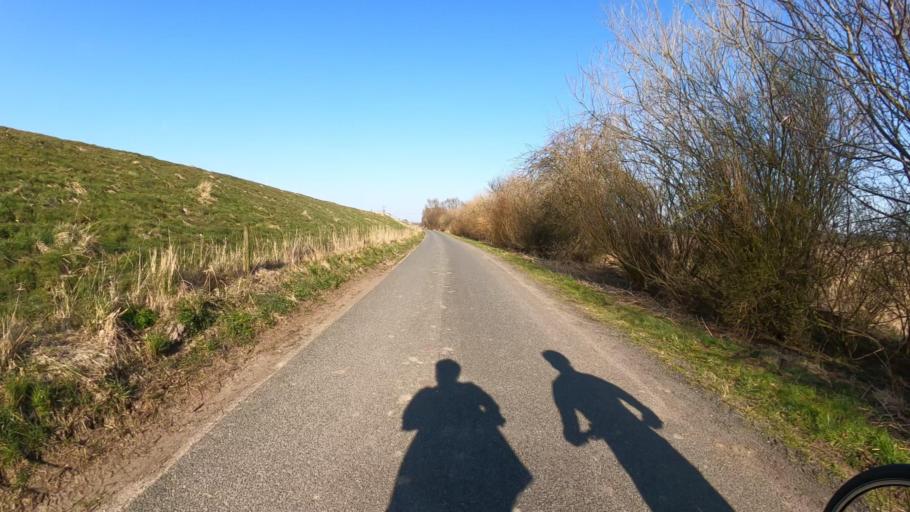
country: DE
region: Schleswig-Holstein
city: Seester
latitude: 53.7296
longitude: 9.6015
